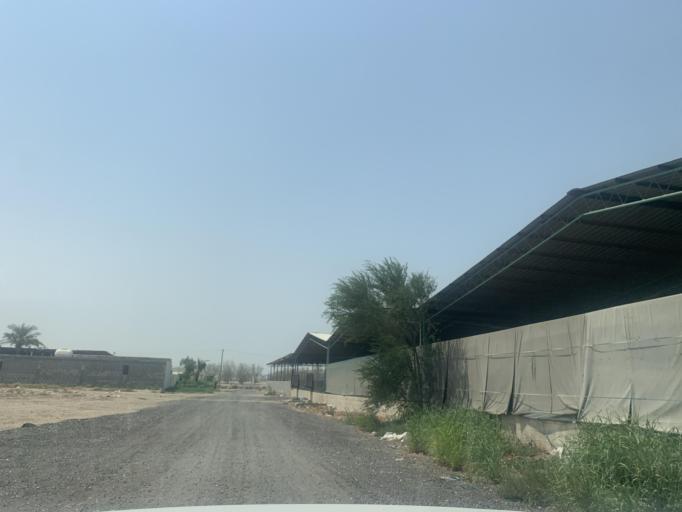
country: BH
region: Central Governorate
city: Madinat Hamad
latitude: 26.1418
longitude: 50.4791
